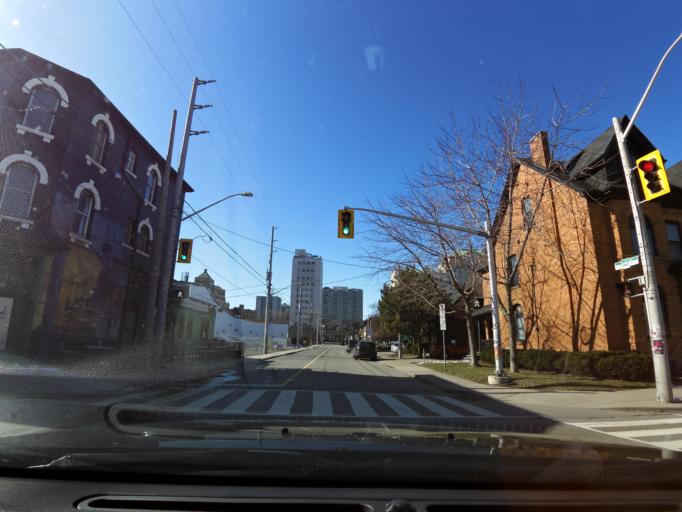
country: CA
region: Ontario
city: Hamilton
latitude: 43.2516
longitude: -79.8683
